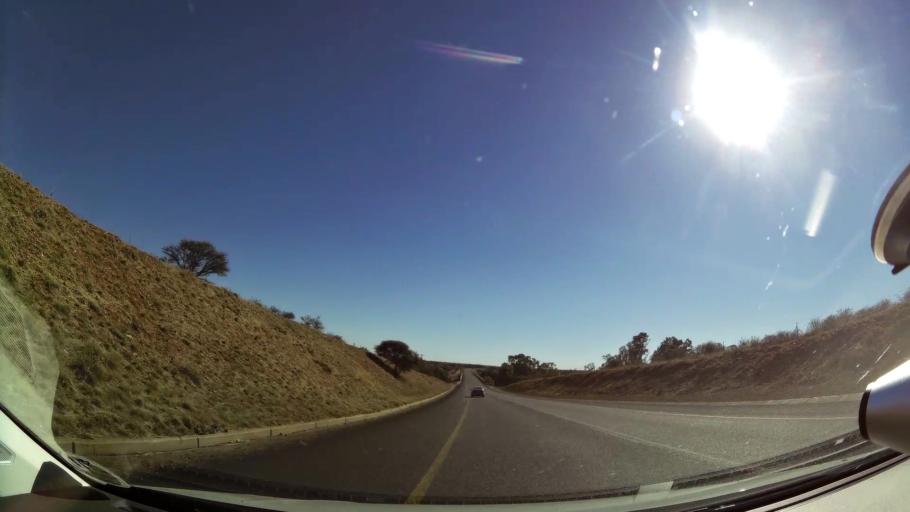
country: ZA
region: Northern Cape
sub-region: Frances Baard District Municipality
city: Warrenton
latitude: -28.0988
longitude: 24.8683
